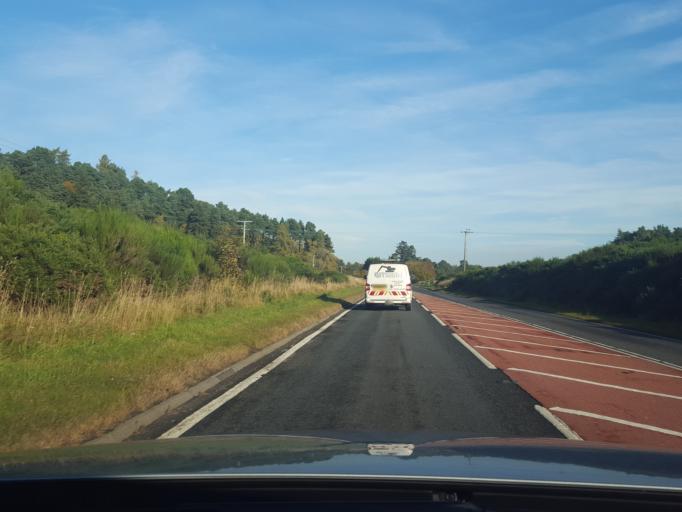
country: GB
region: Scotland
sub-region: Highland
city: Inverness
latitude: 57.4513
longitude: -4.2813
